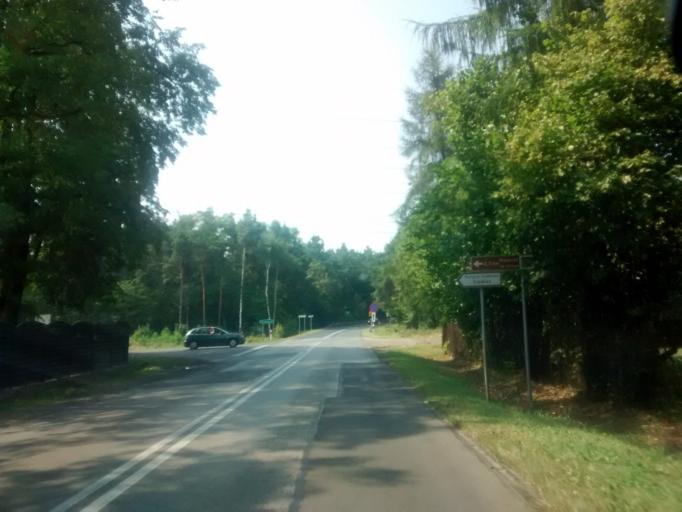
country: PL
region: Silesian Voivodeship
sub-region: Powiat czestochowski
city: Olsztyn
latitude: 50.7430
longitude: 19.3295
